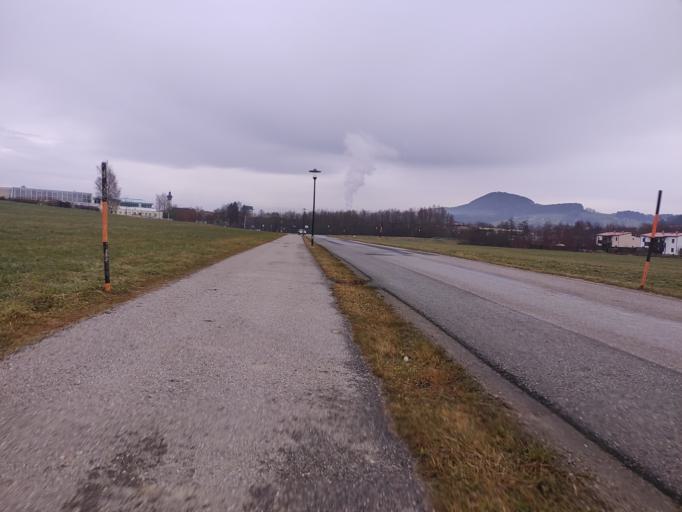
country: AT
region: Salzburg
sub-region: Politischer Bezirk Salzburg-Umgebung
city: Obertrum am See
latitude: 47.9307
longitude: 13.0759
